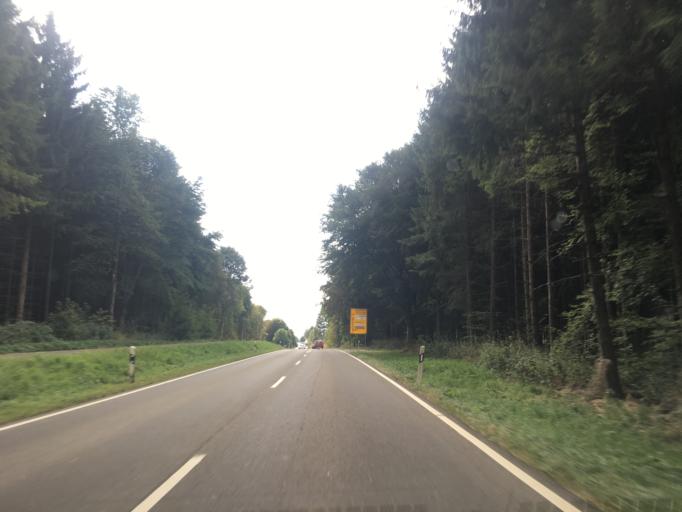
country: DE
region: Baden-Wuerttemberg
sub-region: Tuebingen Region
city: Trochtelfingen
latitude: 48.3669
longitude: 9.2562
